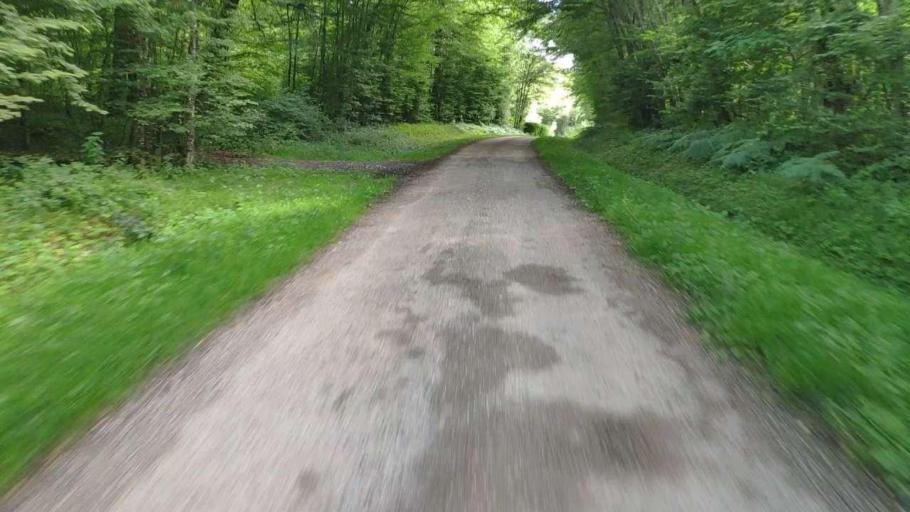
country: FR
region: Franche-Comte
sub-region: Departement du Jura
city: Bletterans
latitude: 46.8206
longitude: 5.5227
